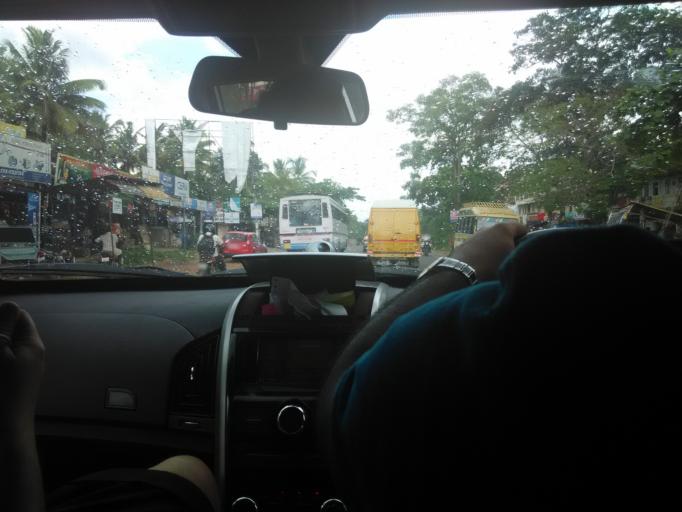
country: IN
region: Kerala
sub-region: Thiruvananthapuram
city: Attingal
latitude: 8.6480
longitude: 76.8420
